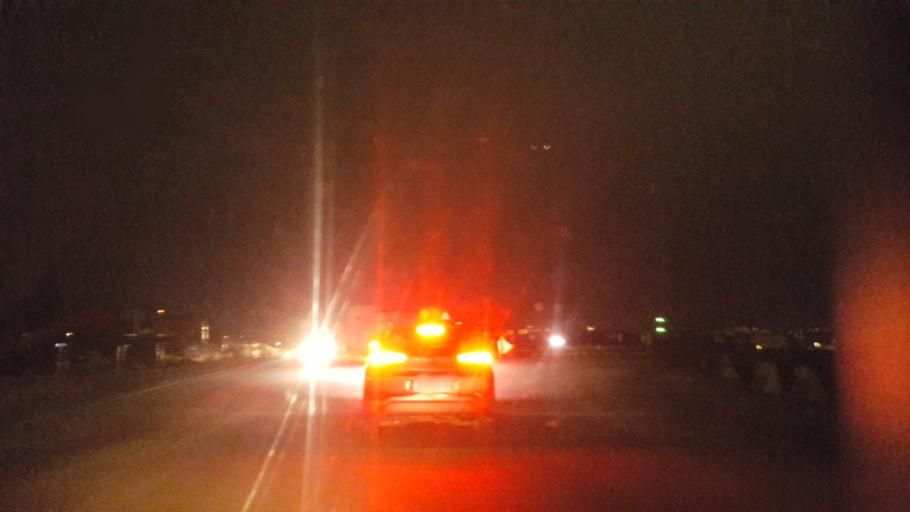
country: TR
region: Istanbul
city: Icmeler
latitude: 40.8346
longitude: 29.3262
